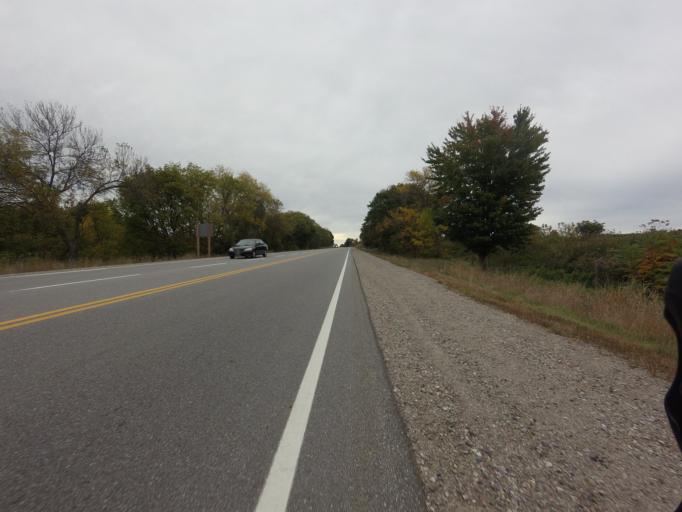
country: CA
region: Ontario
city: Gananoque
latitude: 44.4737
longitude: -76.2352
